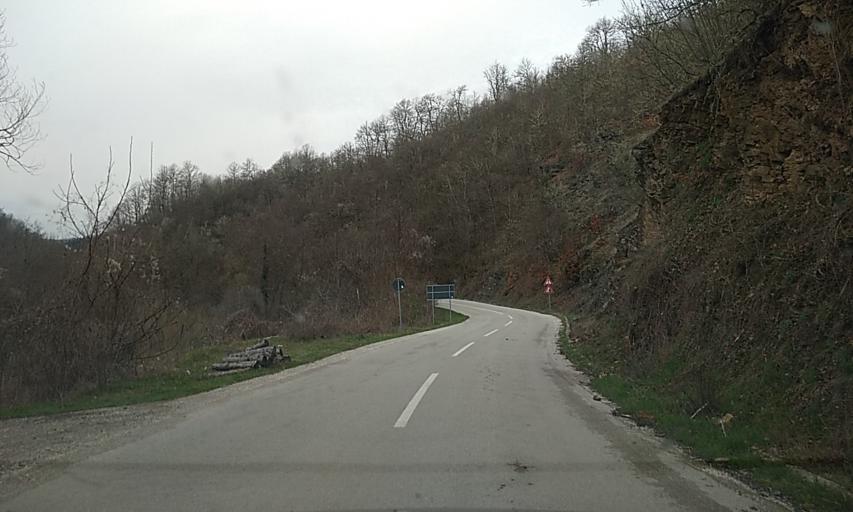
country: RS
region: Central Serbia
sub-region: Pcinjski Okrug
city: Bosilegrad
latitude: 42.4134
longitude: 22.4847
